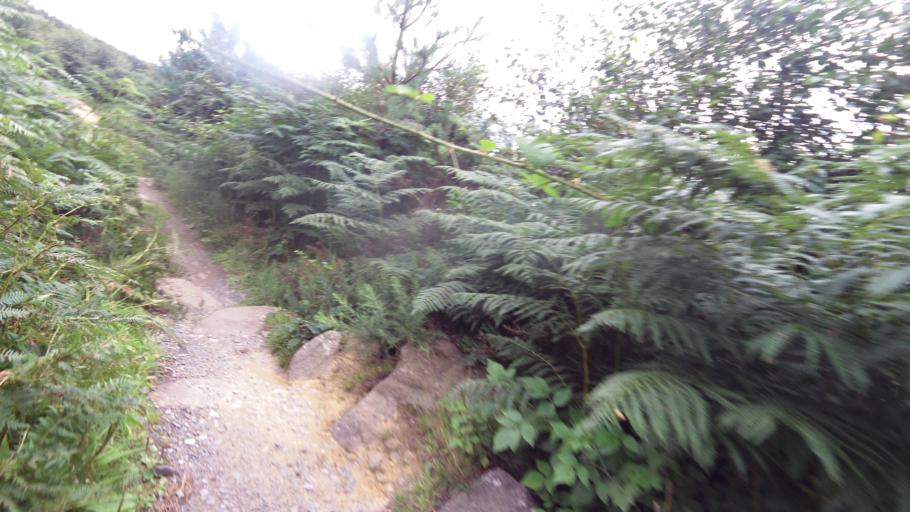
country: GB
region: England
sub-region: City and Borough of Leeds
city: Otley
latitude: 53.9547
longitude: -1.6845
